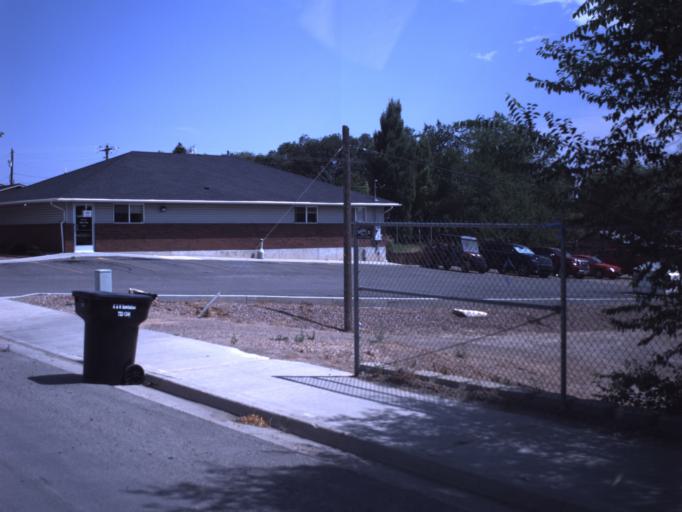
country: US
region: Utah
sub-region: Duchesne County
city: Roosevelt
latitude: 40.3021
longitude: -109.9964
